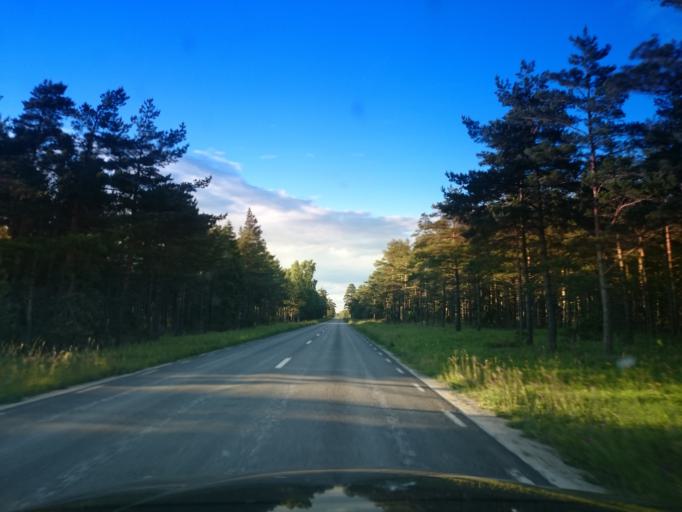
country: SE
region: Gotland
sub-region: Gotland
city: Hemse
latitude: 57.3429
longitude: 18.3800
